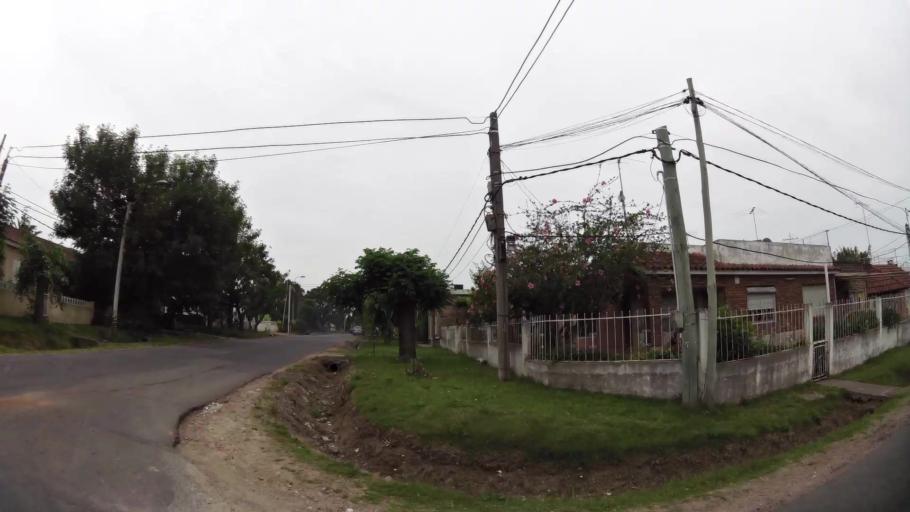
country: UY
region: Canelones
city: Las Piedras
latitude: -34.7364
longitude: -56.2276
